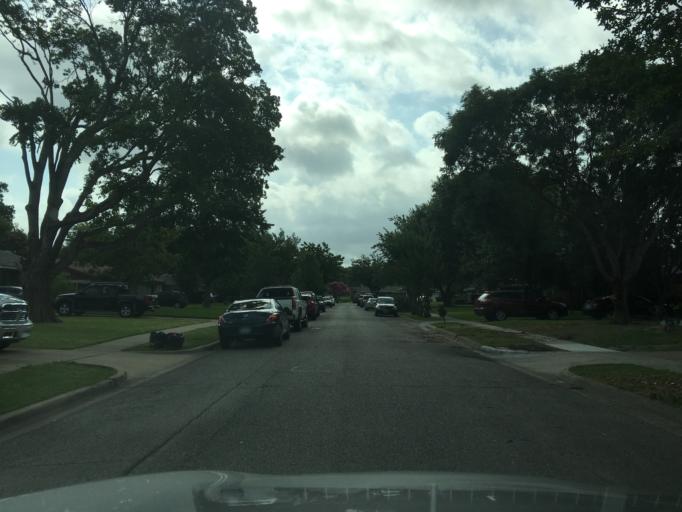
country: US
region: Texas
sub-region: Dallas County
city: Richardson
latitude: 32.9502
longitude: -96.7175
